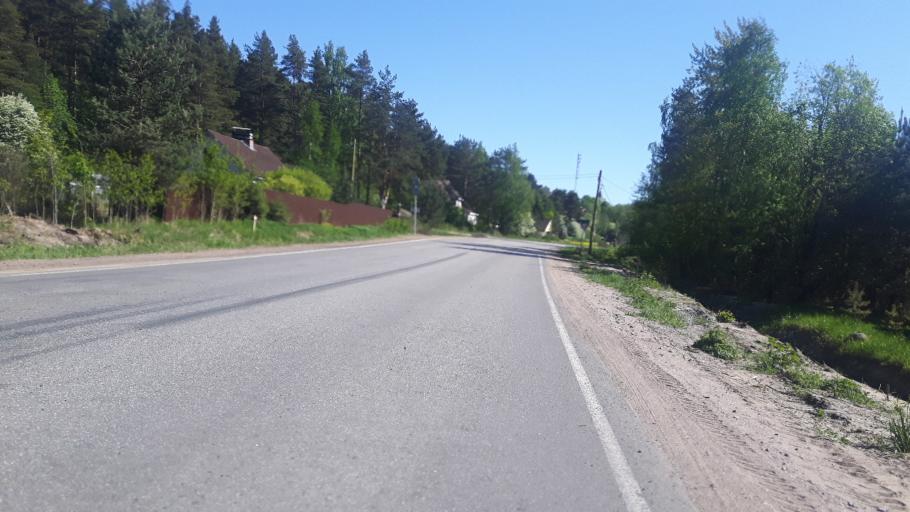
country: RU
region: Leningrad
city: Sosnovyy Bor
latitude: 60.2221
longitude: 29.0088
